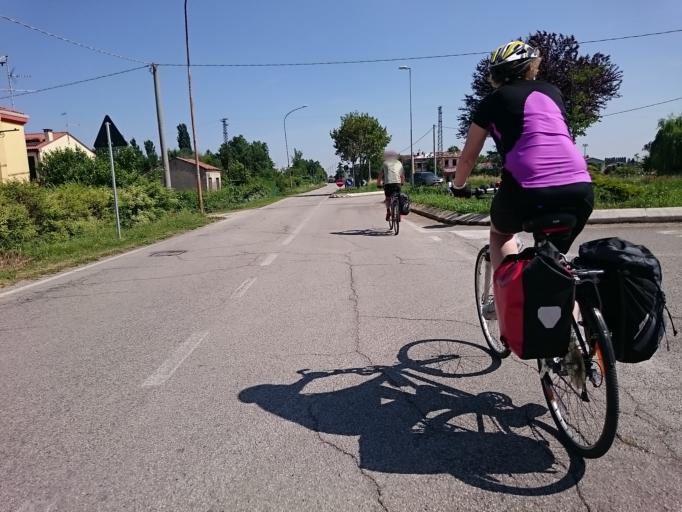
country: IT
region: Veneto
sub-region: Provincia di Padova
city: Montagnana
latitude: 45.2409
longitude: 11.4733
